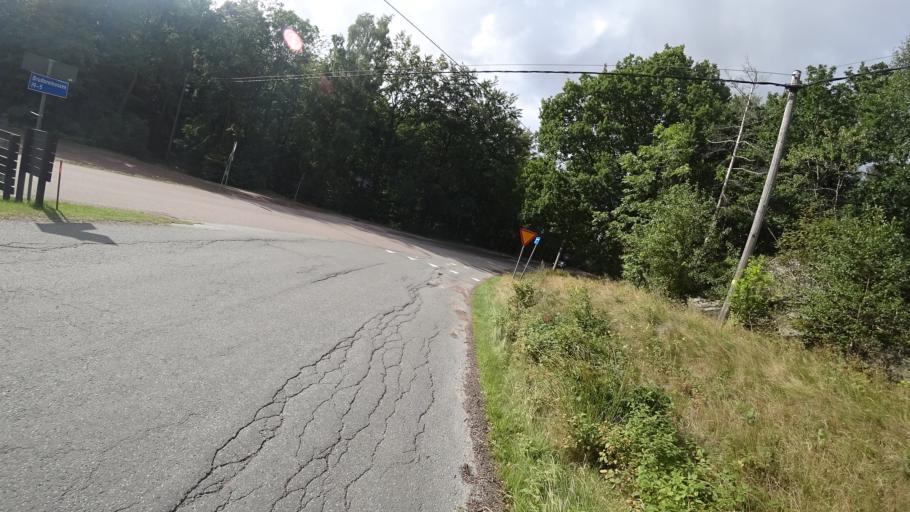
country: SE
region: Vaestra Goetaland
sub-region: Molndal
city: Moelndal
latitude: 57.6987
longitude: 12.0332
